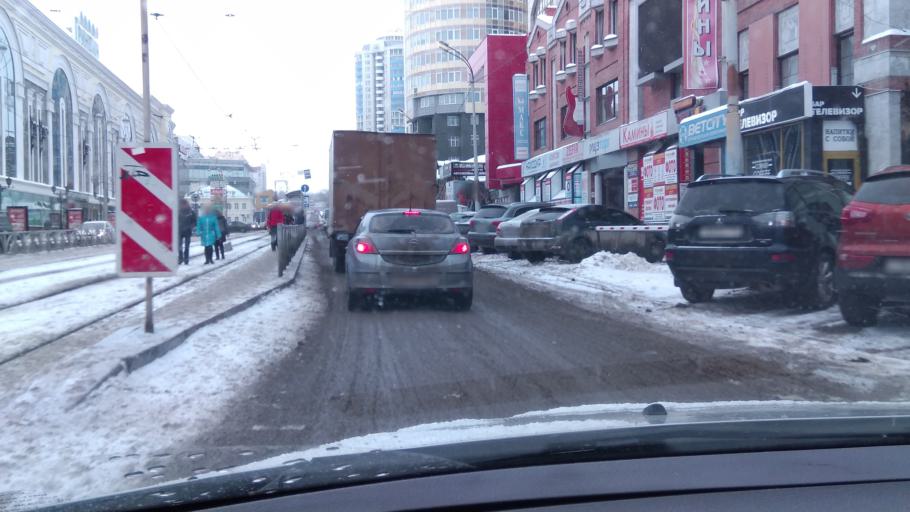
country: RU
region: Sverdlovsk
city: Yekaterinburg
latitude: 56.8307
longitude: 60.6005
